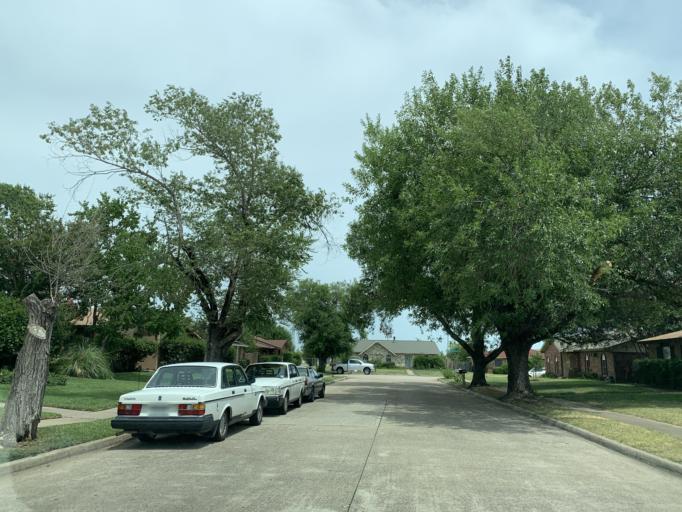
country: US
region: Texas
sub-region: Dallas County
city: Grand Prairie
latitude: 32.6552
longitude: -97.0327
